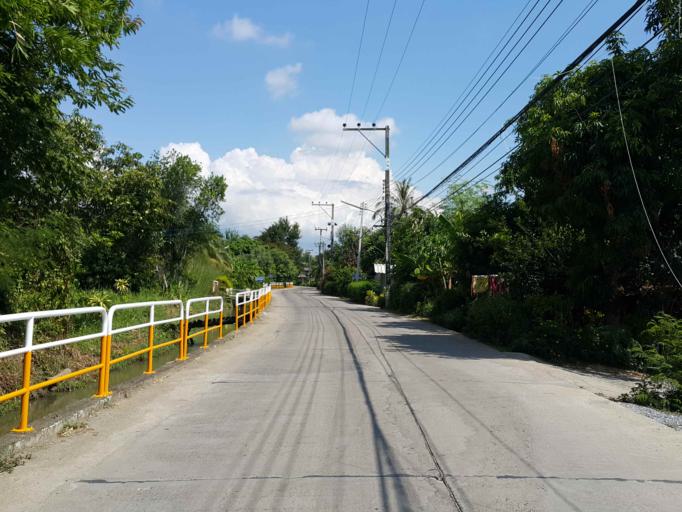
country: TH
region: Chiang Mai
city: Saraphi
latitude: 18.7279
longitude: 99.0447
